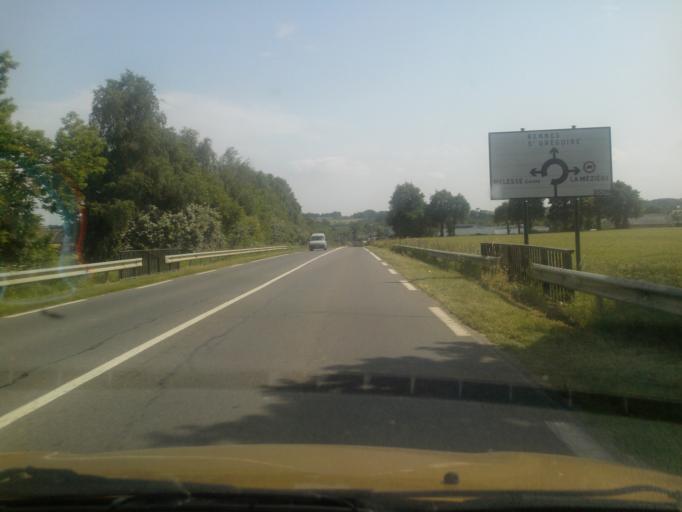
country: FR
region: Brittany
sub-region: Departement d'Ille-et-Vilaine
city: Melesse
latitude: 48.2195
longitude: -1.7034
